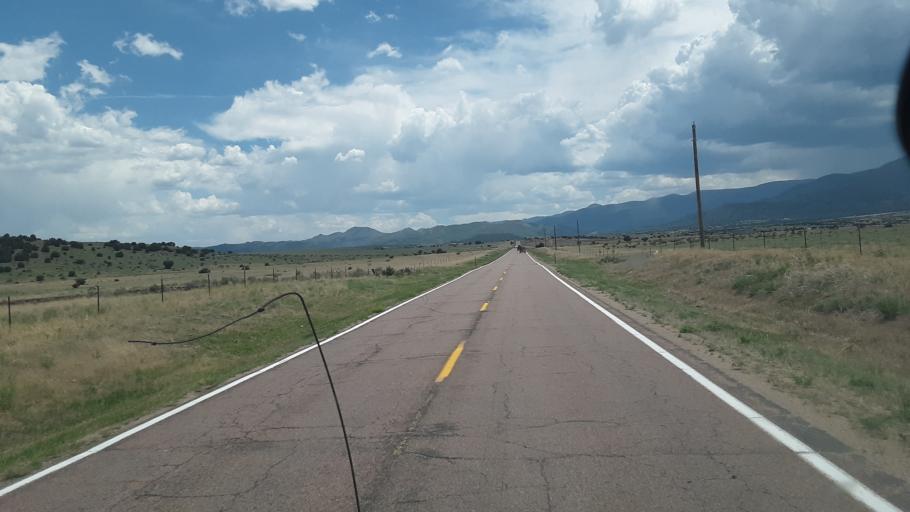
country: US
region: Colorado
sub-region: Fremont County
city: Florence
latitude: 38.2832
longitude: -105.0874
